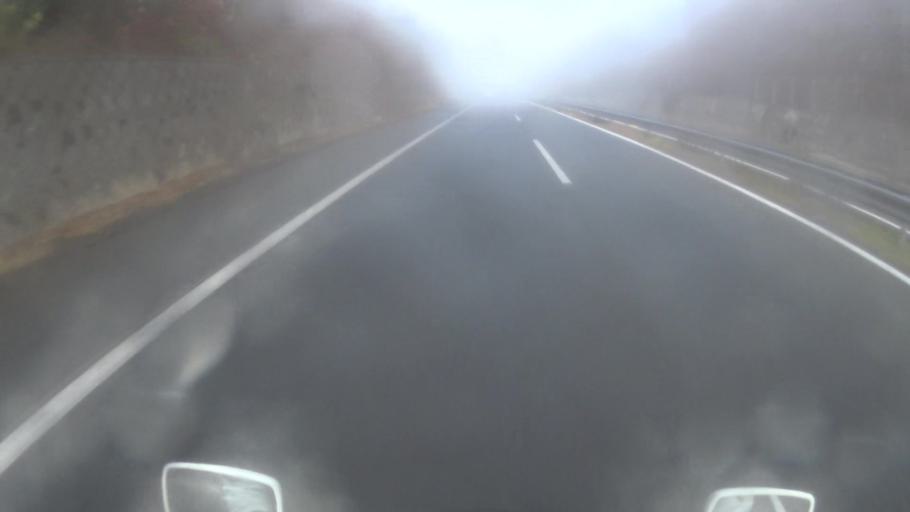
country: JP
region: Kyoto
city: Kameoka
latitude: 35.0987
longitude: 135.4956
